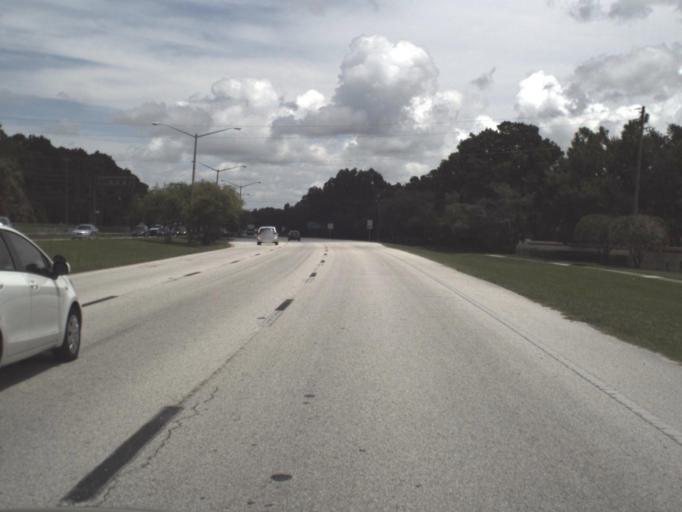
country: US
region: Florida
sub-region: Pinellas County
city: East Lake
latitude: 28.0836
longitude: -82.7004
